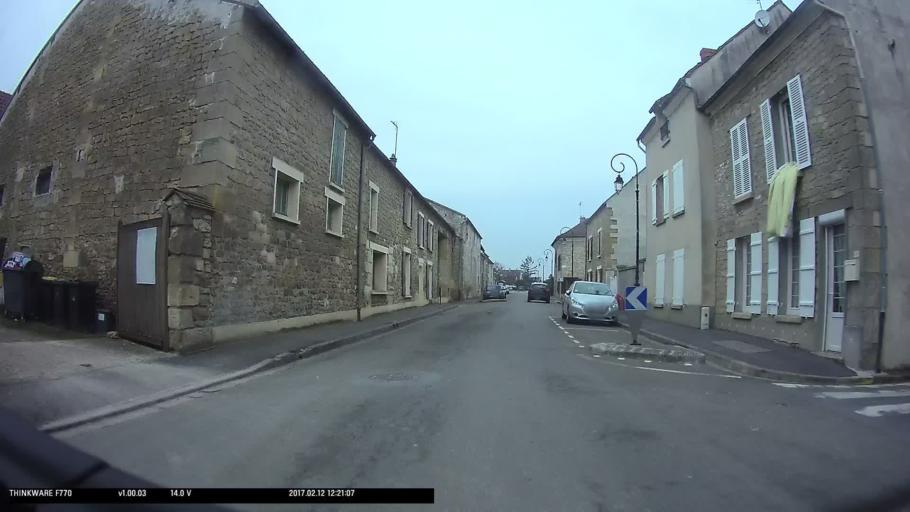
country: FR
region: Ile-de-France
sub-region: Departement du Val-d'Oise
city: Sagy
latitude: 49.0683
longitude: 1.9670
